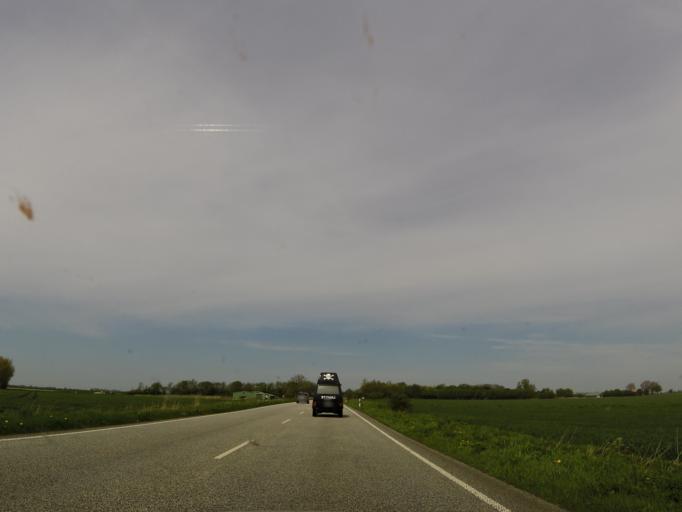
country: DE
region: Schleswig-Holstein
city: Groven
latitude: 54.2960
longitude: 8.9732
